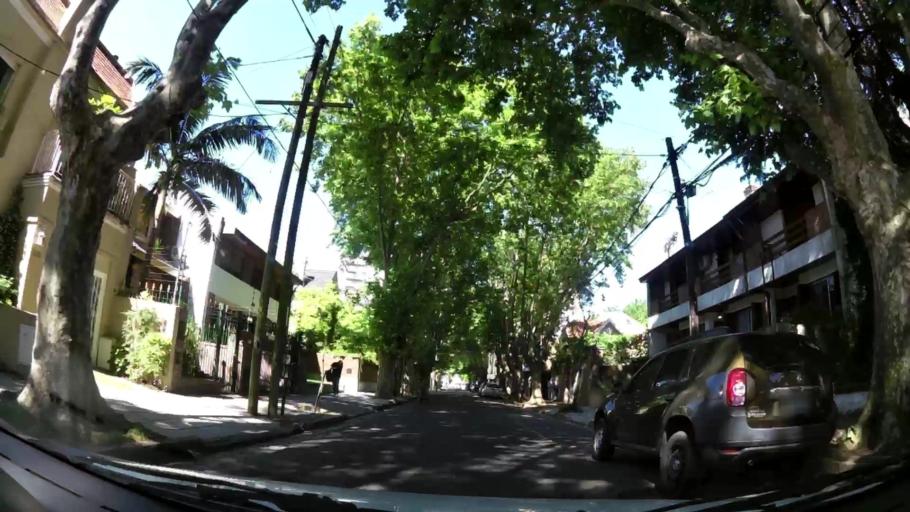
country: AR
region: Buenos Aires
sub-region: Partido de Vicente Lopez
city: Olivos
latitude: -34.5257
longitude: -58.4803
